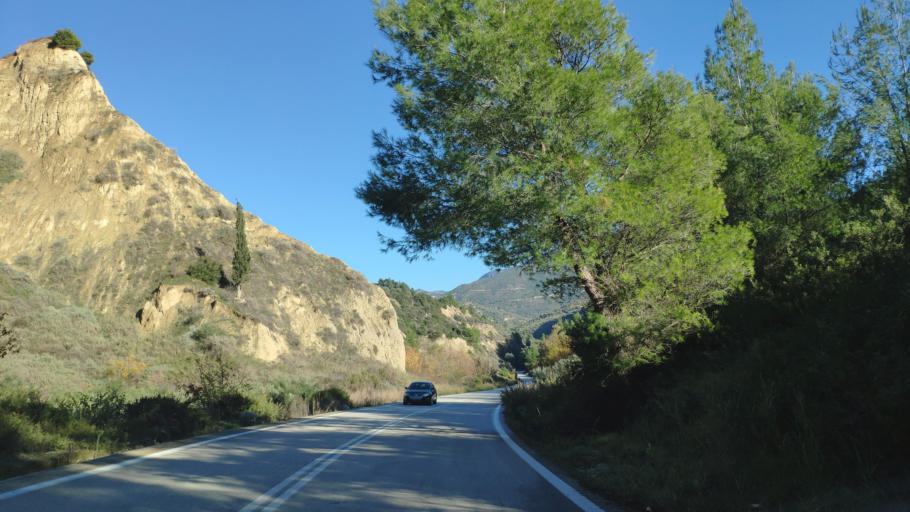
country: GR
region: Peloponnese
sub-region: Nomos Korinthias
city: Xylokastro
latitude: 38.0091
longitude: 22.5238
